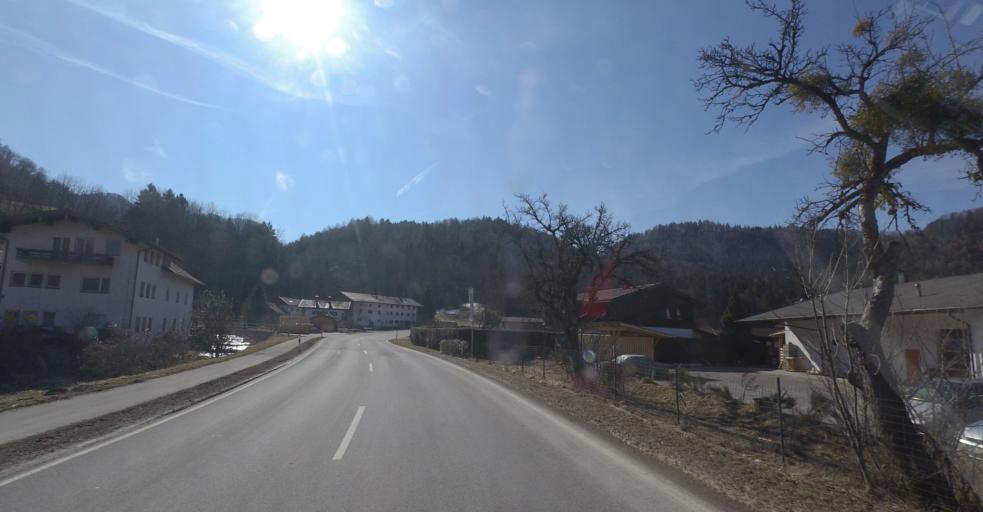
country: DE
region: Bavaria
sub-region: Upper Bavaria
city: Unterwossen
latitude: 47.7253
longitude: 12.4681
